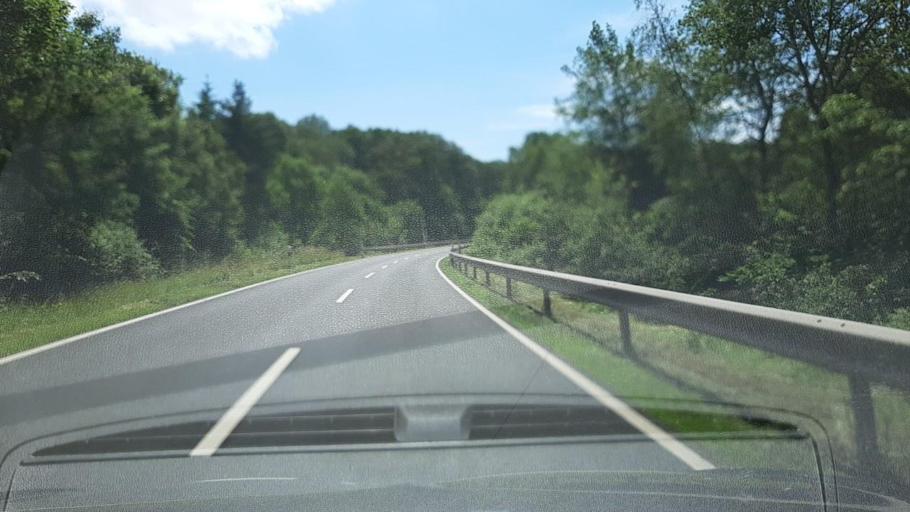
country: DE
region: Rheinland-Pfalz
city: Ediger-Eller
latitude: 50.1118
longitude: 7.1728
